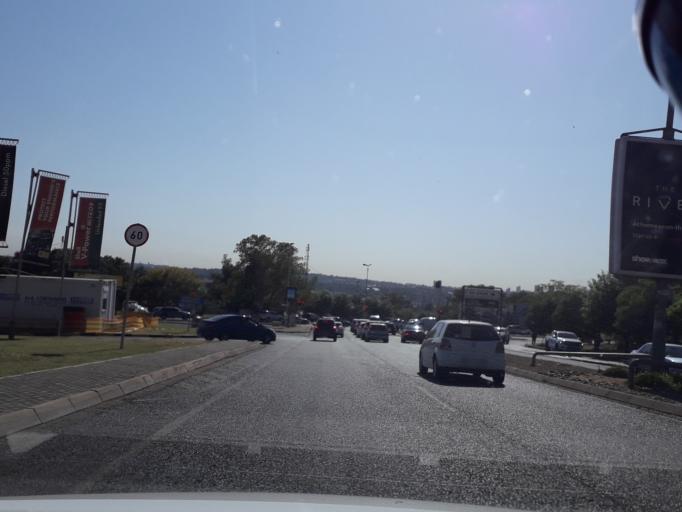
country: ZA
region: Gauteng
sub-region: City of Johannesburg Metropolitan Municipality
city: Roodepoort
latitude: -26.0919
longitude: 27.9589
